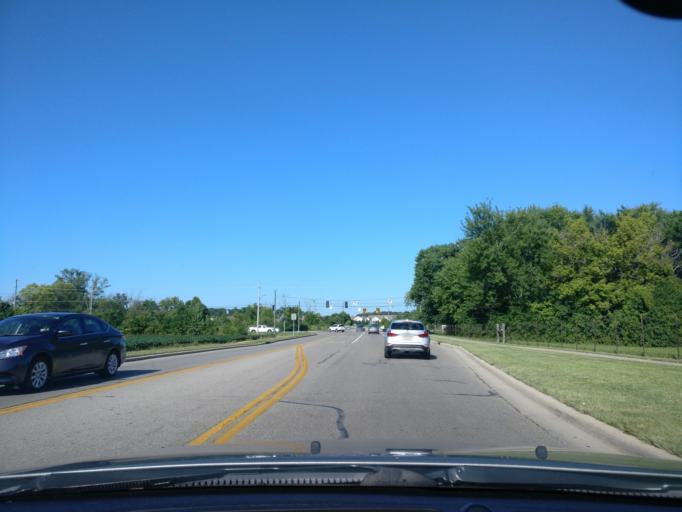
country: US
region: Ohio
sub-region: Montgomery County
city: Centerville
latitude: 39.6146
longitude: -84.1973
